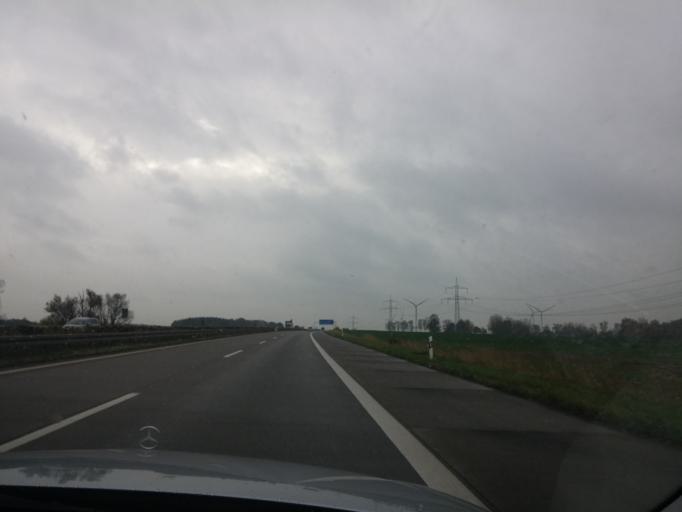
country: DE
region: Mecklenburg-Vorpommern
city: Roggentin
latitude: 54.0476
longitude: 12.1992
